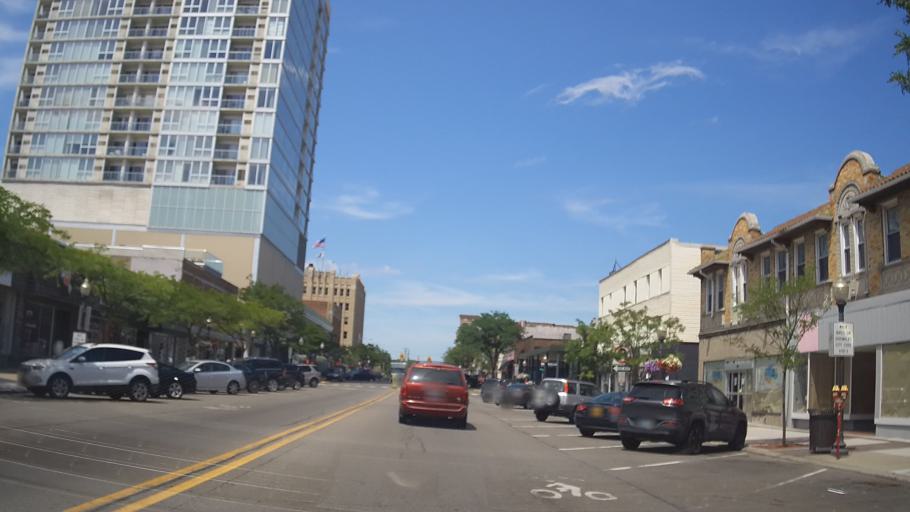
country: US
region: Michigan
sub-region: Oakland County
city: Royal Oak
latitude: 42.4856
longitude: -83.1465
